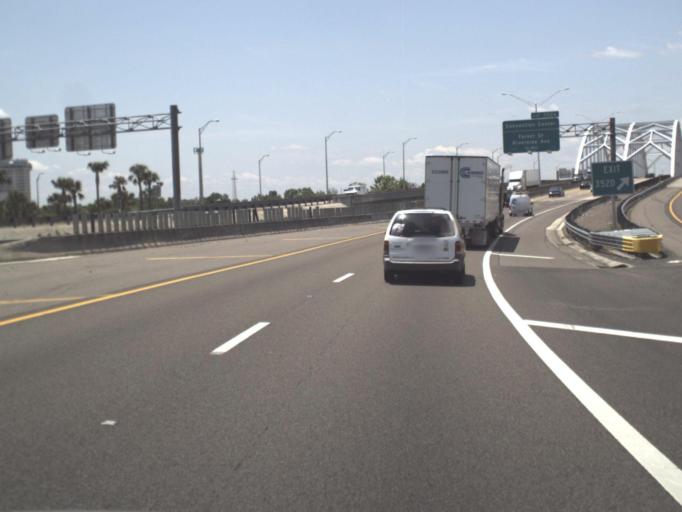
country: US
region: Florida
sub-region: Duval County
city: Jacksonville
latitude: 30.3313
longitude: -81.6740
